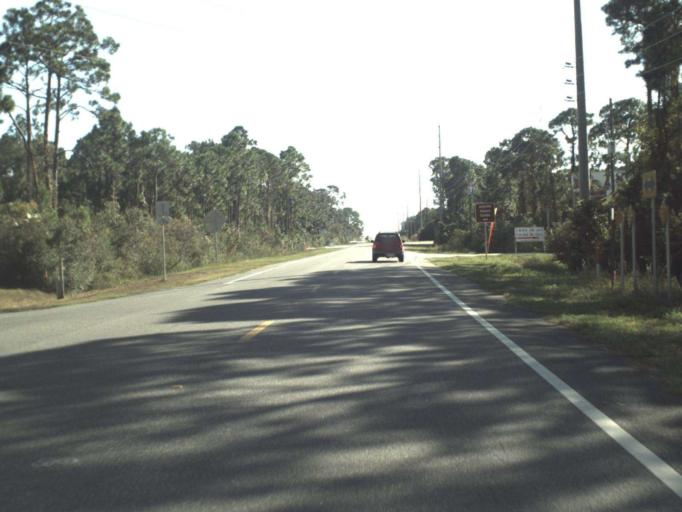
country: US
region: Florida
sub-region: Franklin County
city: Eastpoint
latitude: 29.7306
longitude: -84.8880
